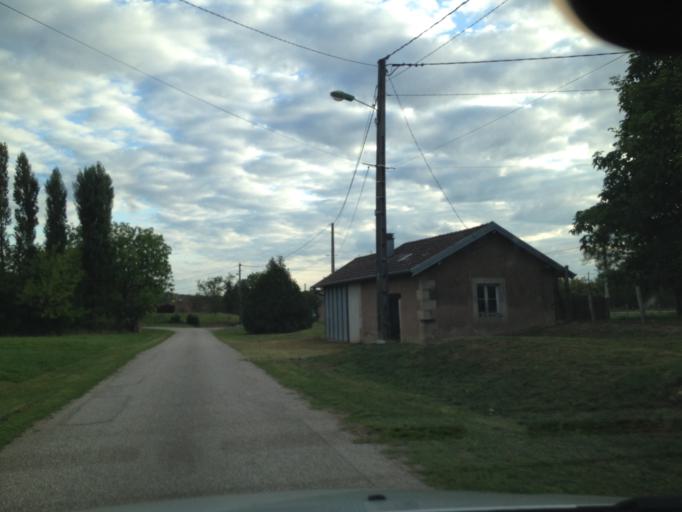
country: FR
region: Lorraine
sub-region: Departement des Vosges
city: Bains-les-Bains
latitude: 47.9758
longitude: 6.1772
